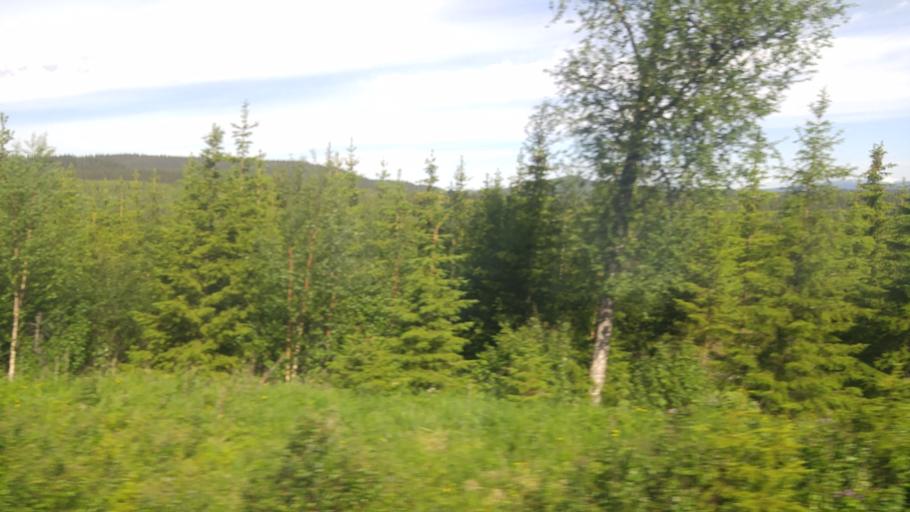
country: SE
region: Jaemtland
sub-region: Are Kommun
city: Are
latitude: 63.3932
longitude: 12.7944
